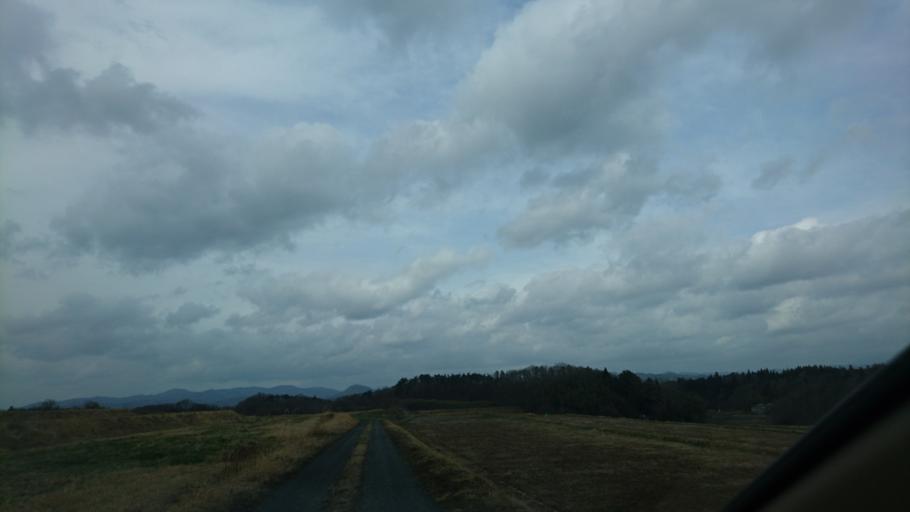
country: JP
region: Iwate
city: Ichinoseki
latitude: 38.8897
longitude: 141.1622
